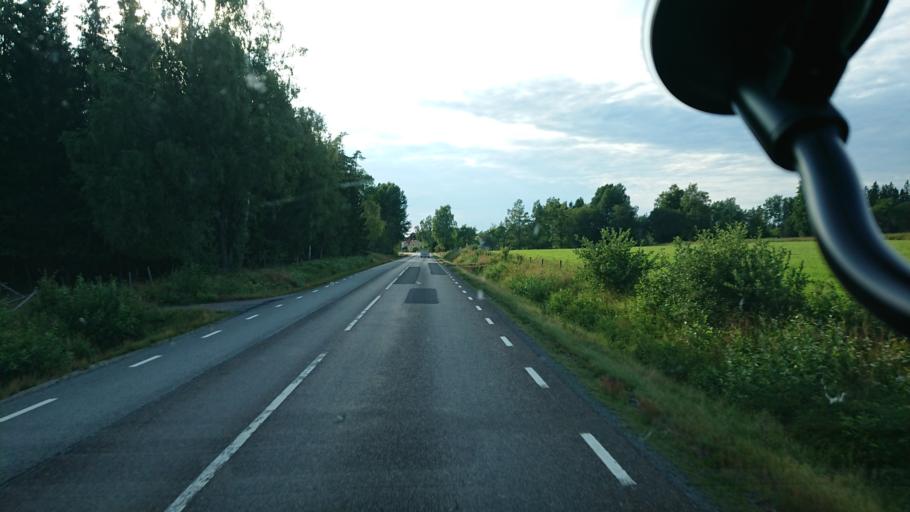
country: SE
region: Kronoberg
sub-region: Vaxjo Kommun
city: Braas
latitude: 57.0195
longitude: 15.0425
